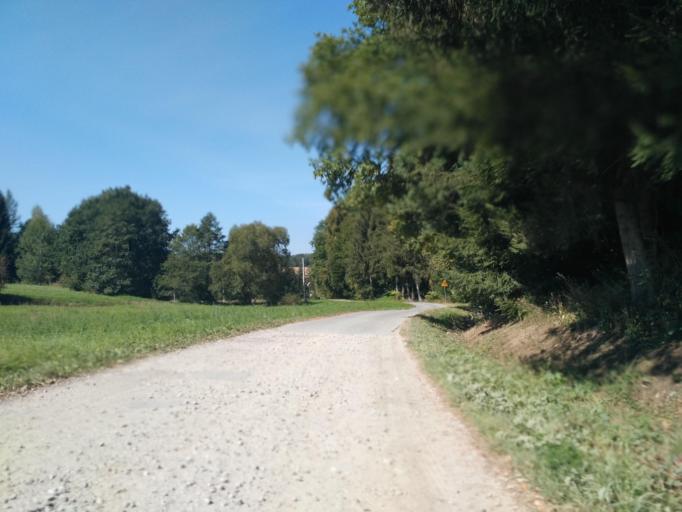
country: PL
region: Subcarpathian Voivodeship
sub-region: Powiat brzozowski
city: Niebocko
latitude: 49.6395
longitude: 22.1341
